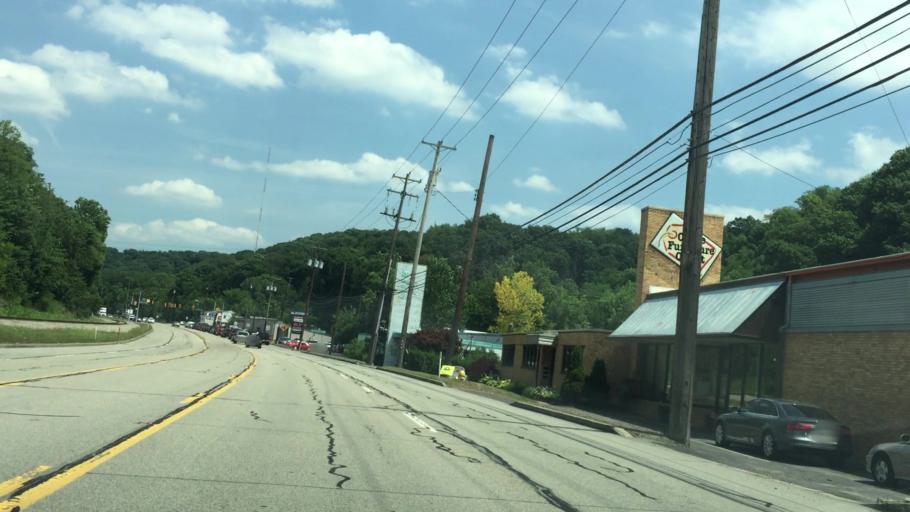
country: US
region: Pennsylvania
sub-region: Allegheny County
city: Allison Park
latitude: 40.5473
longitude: -79.9607
